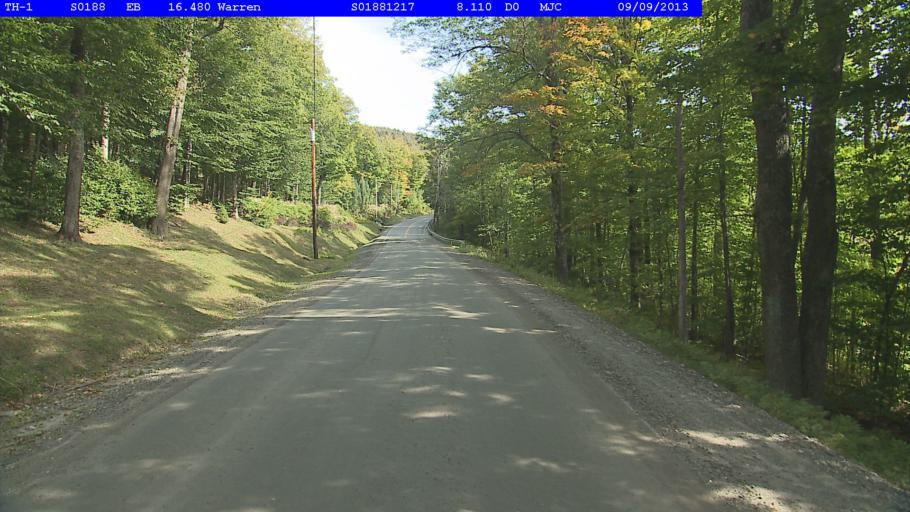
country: US
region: Vermont
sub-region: Washington County
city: Northfield
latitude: 44.1055
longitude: -72.7956
